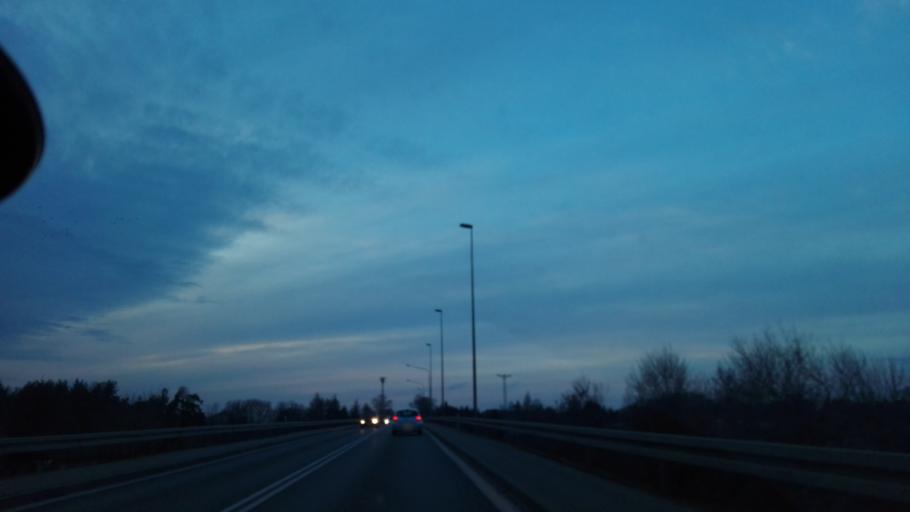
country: PL
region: Masovian Voivodeship
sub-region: Powiat siedlecki
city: Skorzec
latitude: 52.1768
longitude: 22.1865
